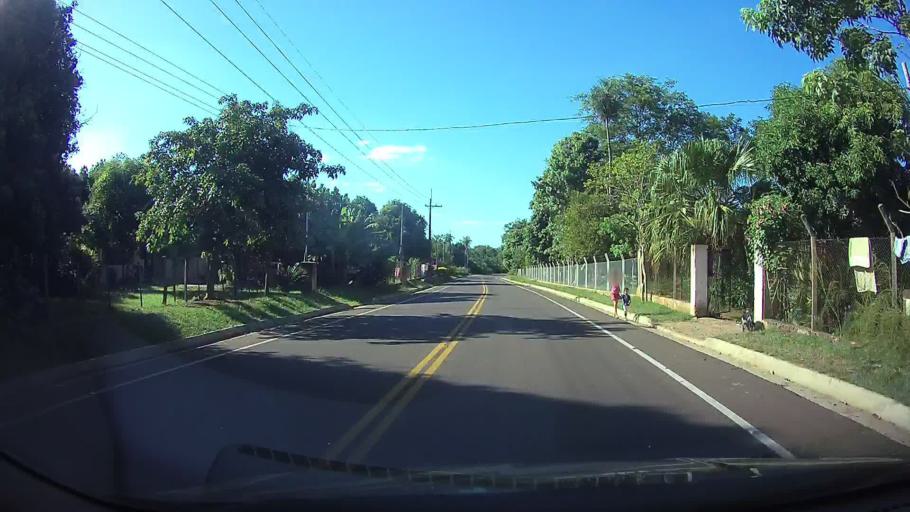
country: PY
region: Cordillera
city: Caacupe
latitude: -25.3410
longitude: -57.1545
